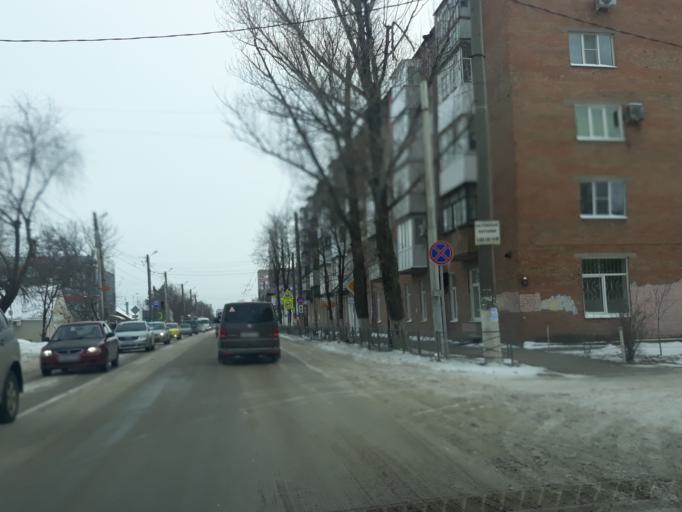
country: RU
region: Rostov
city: Taganrog
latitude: 47.2215
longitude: 38.8880
